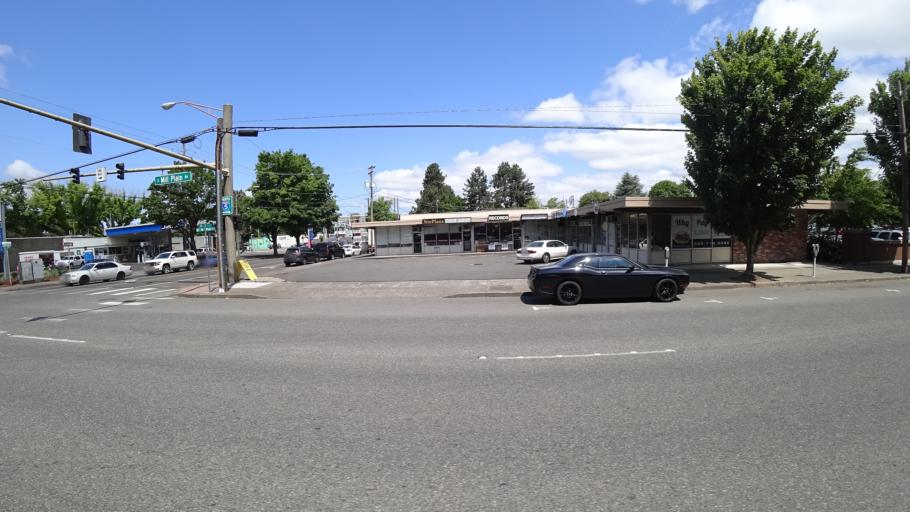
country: US
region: Washington
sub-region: Clark County
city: Vancouver
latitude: 45.6318
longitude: -122.6692
